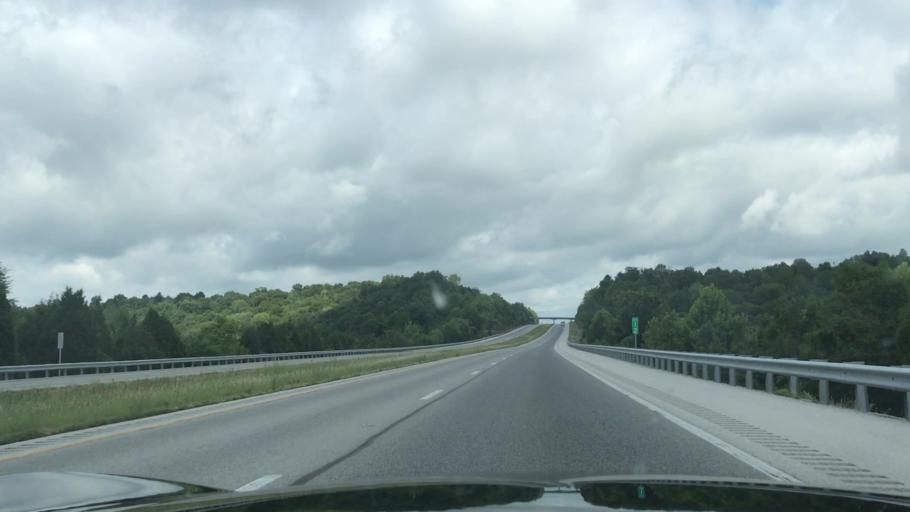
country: US
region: Kentucky
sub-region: Warren County
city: Bowling Green
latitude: 37.0214
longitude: -86.5270
